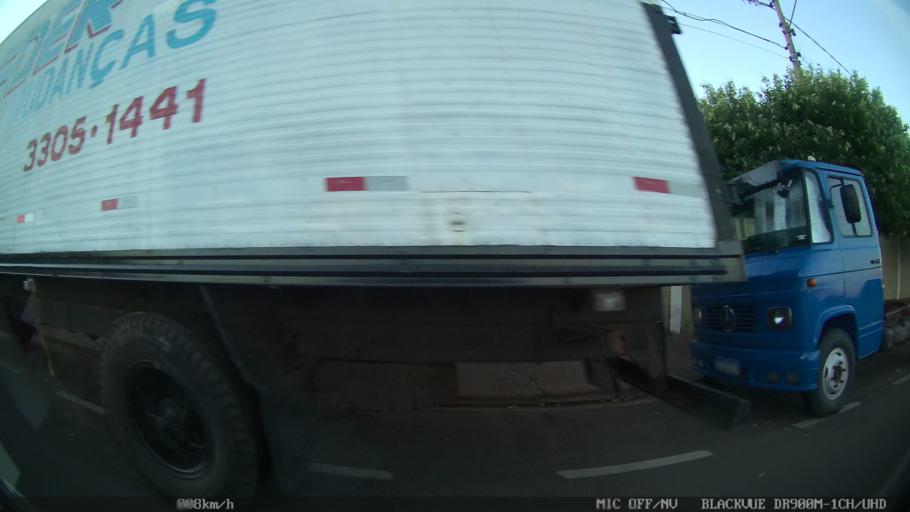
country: BR
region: Sao Paulo
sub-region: Sao Jose Do Rio Preto
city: Sao Jose do Rio Preto
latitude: -20.8440
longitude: -49.3827
